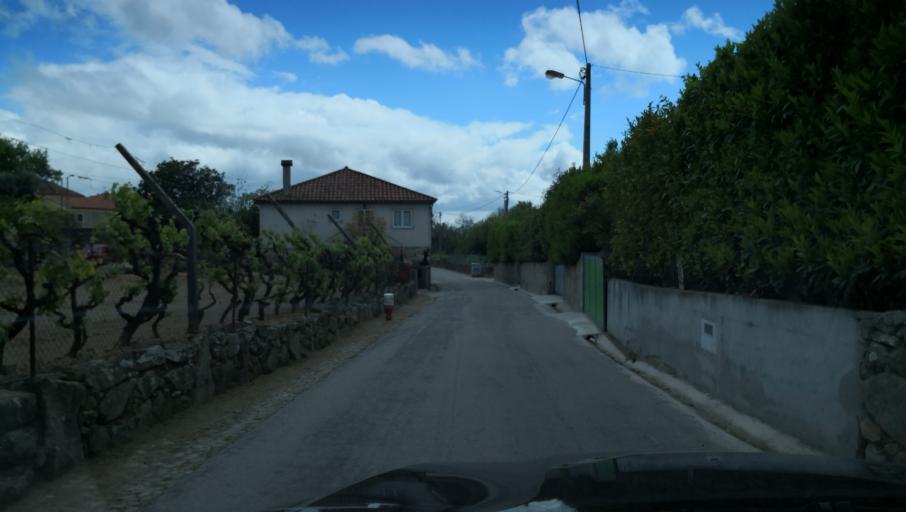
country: PT
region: Vila Real
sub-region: Vila Real
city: Vila Real
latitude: 41.3353
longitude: -7.7256
